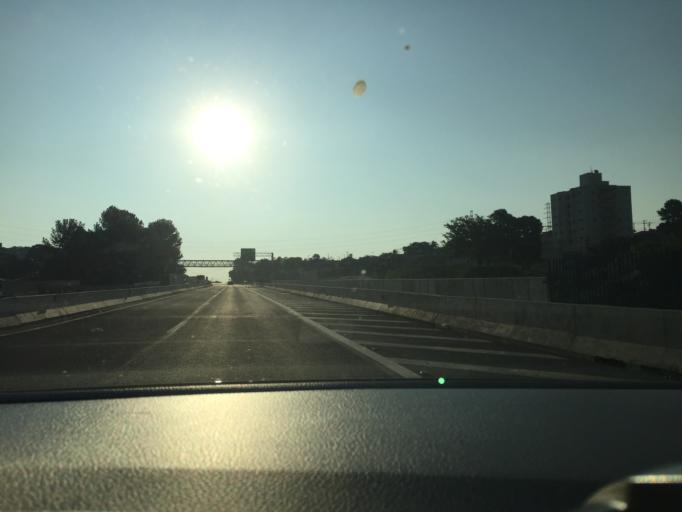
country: BR
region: Sao Paulo
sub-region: Louveira
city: Louveira
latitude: -23.0897
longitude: -46.9487
